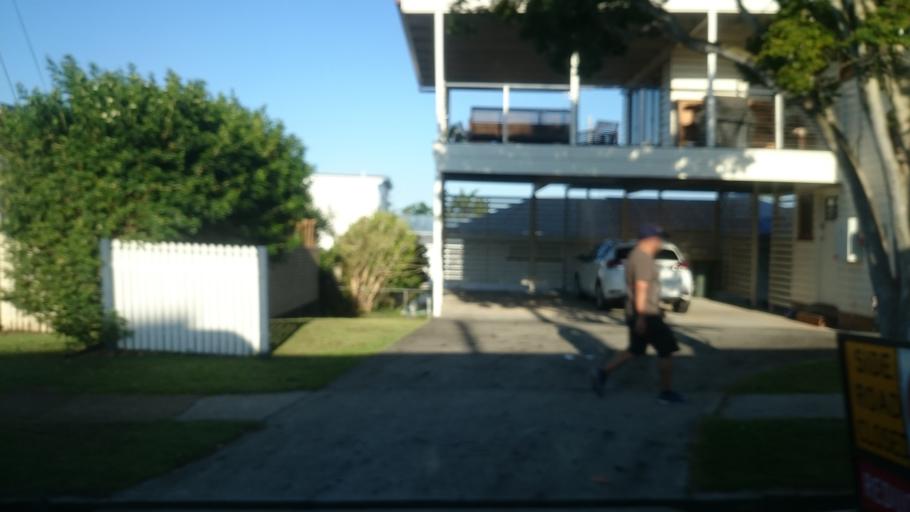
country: AU
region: Queensland
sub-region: Brisbane
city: Manly West
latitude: -27.4548
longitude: 153.1825
